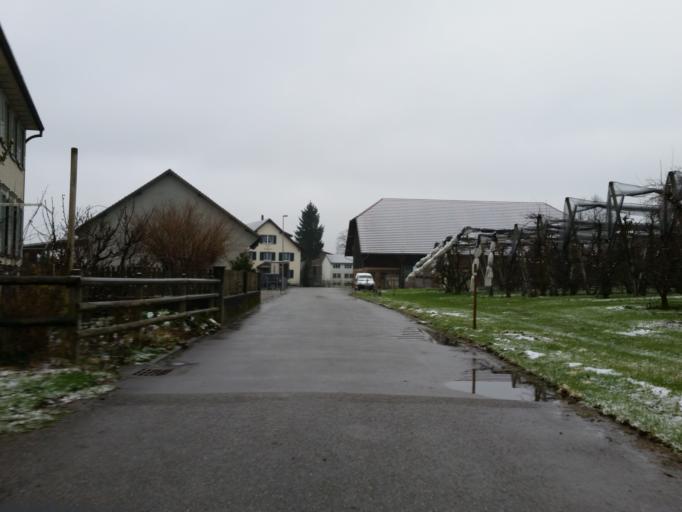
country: CH
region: Thurgau
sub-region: Arbon District
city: Egnach
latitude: 47.5276
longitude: 9.3857
